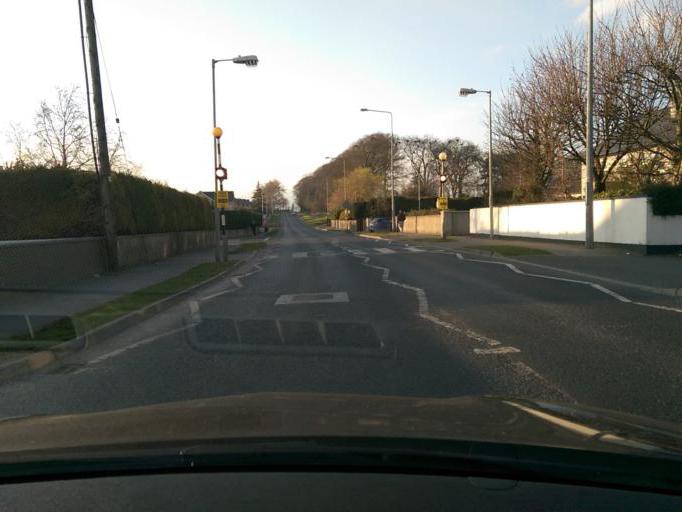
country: IE
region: Munster
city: Nenagh Bridge
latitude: 52.8719
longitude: -8.1973
